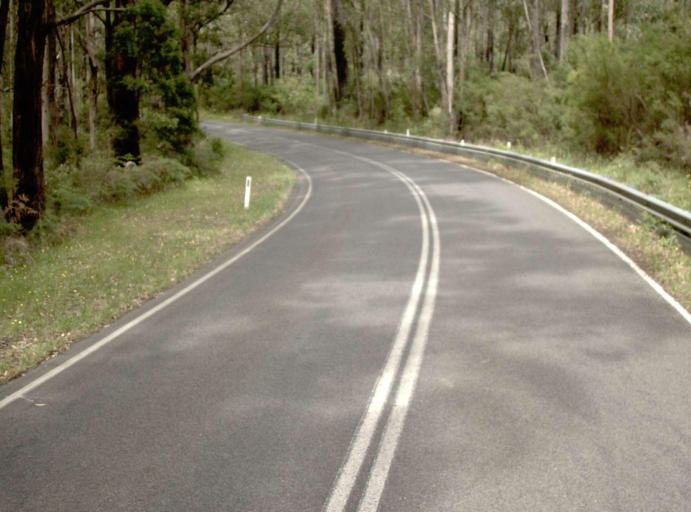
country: AU
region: Victoria
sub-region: Latrobe
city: Morwell
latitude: -38.0495
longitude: 146.4231
